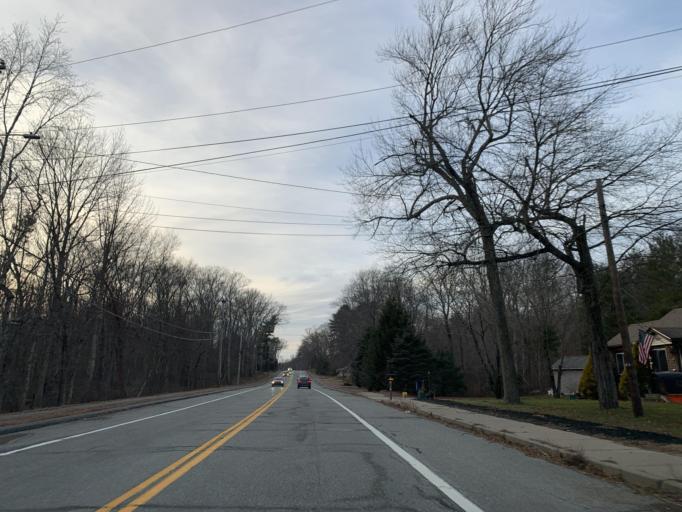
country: US
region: Rhode Island
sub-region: Providence County
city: Chepachet
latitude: 41.9181
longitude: -71.6833
